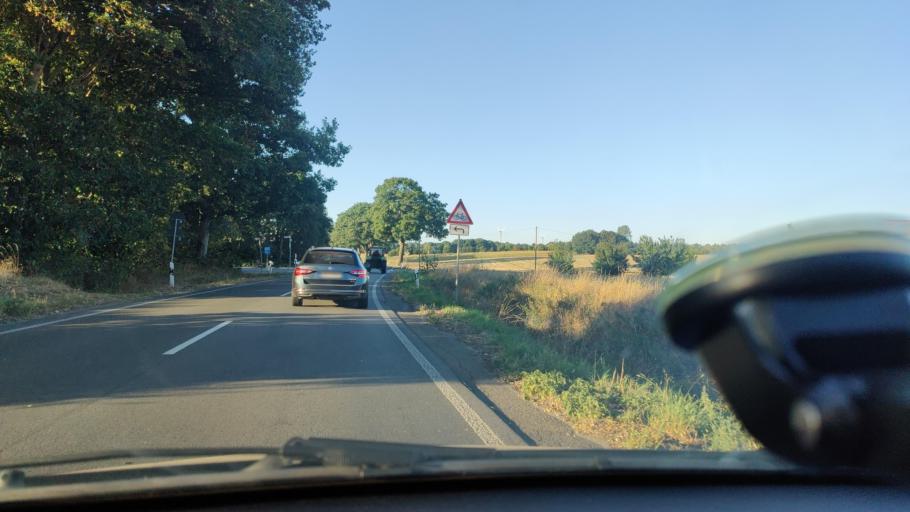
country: DE
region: North Rhine-Westphalia
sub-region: Regierungsbezirk Munster
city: Klein Reken
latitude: 51.7667
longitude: 6.9990
